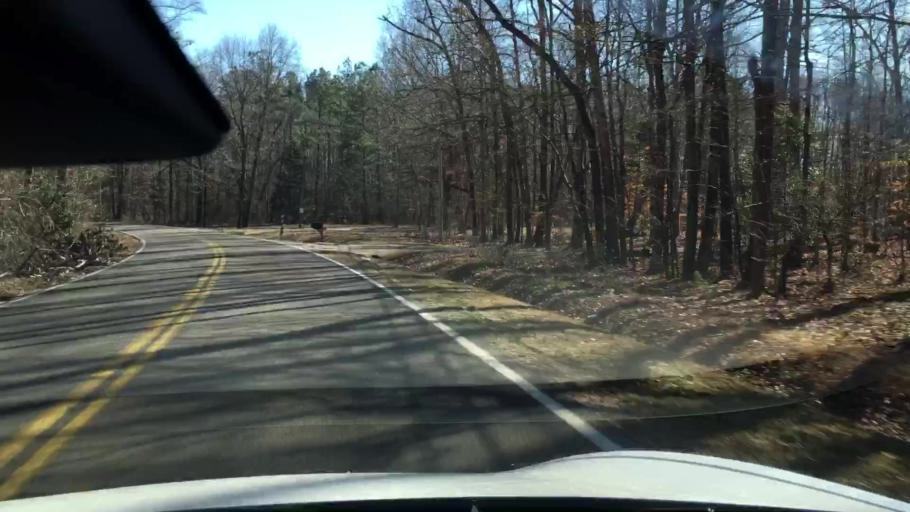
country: US
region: Virginia
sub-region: Henrico County
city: Short Pump
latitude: 37.5787
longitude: -77.7359
